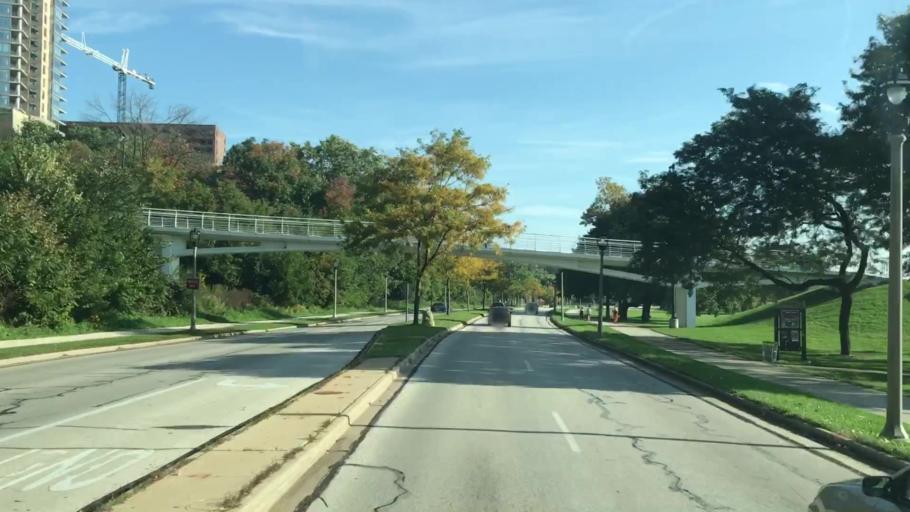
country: US
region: Wisconsin
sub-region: Milwaukee County
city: Milwaukee
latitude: 43.0513
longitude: -87.8899
